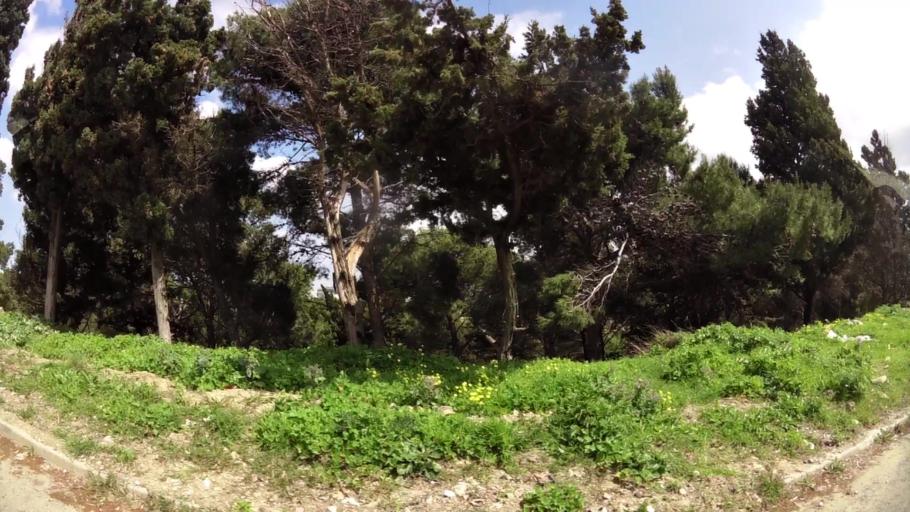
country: MA
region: Tanger-Tetouan
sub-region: Tanger-Assilah
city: Tangier
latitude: 35.7766
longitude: -5.7714
